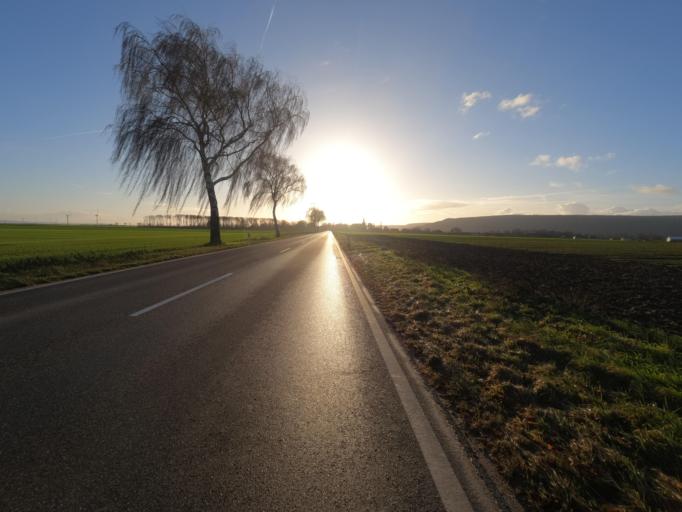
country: DE
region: North Rhine-Westphalia
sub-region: Regierungsbezirk Koln
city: Titz
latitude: 50.9725
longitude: 6.4524
